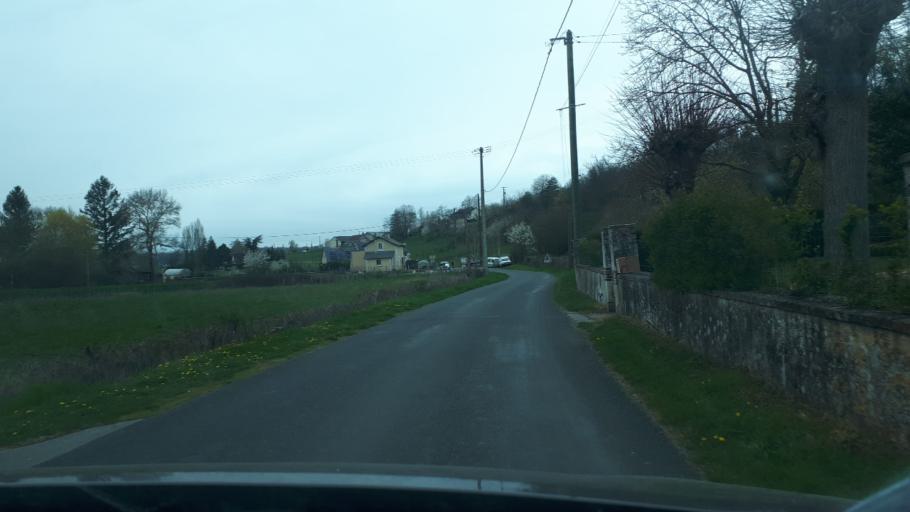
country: FR
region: Centre
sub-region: Departement du Loir-et-Cher
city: Lunay
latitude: 47.7673
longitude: 0.9180
